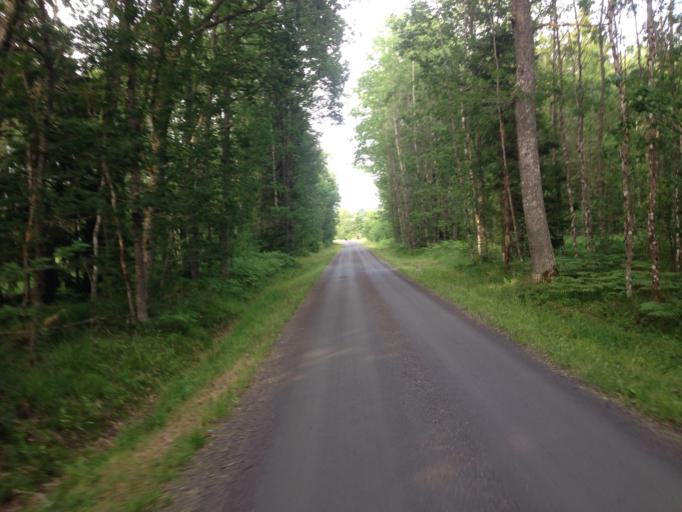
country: SE
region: Kronoberg
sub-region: Ljungby Kommun
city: Ljungby
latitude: 56.8650
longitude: 13.7914
